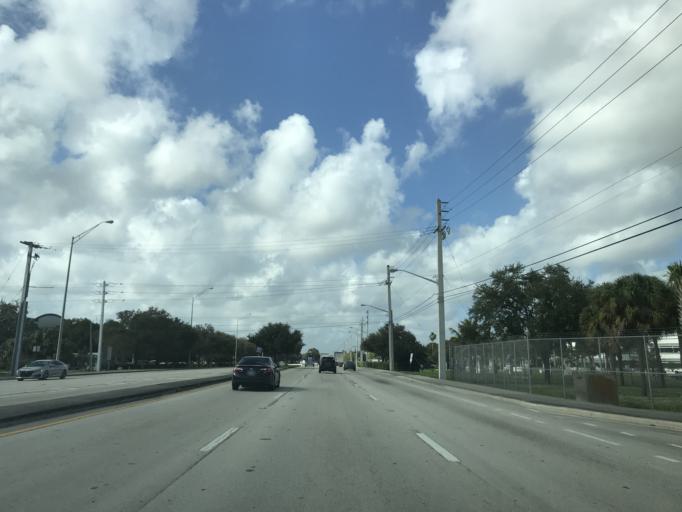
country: US
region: Florida
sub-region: Broward County
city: Coconut Creek
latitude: 26.2602
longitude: -80.1572
